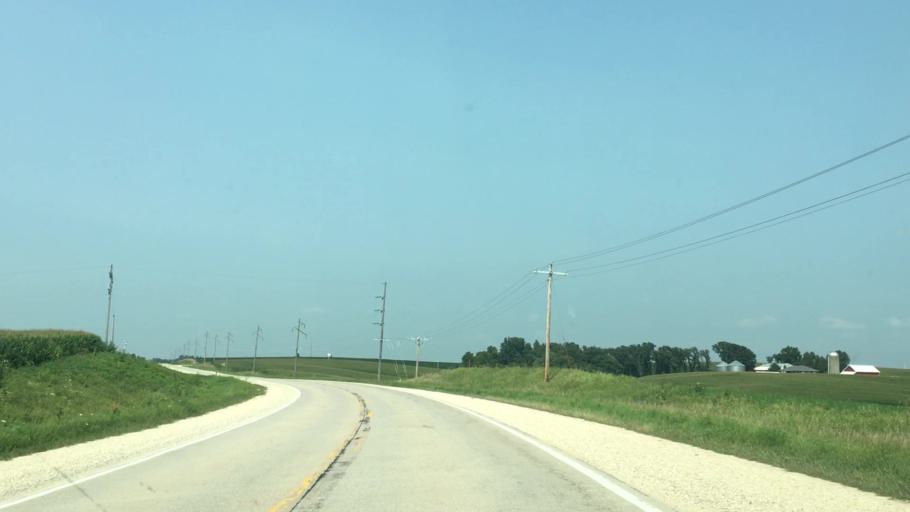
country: US
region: Iowa
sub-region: Winneshiek County
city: Decorah
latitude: 43.1424
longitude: -91.8645
